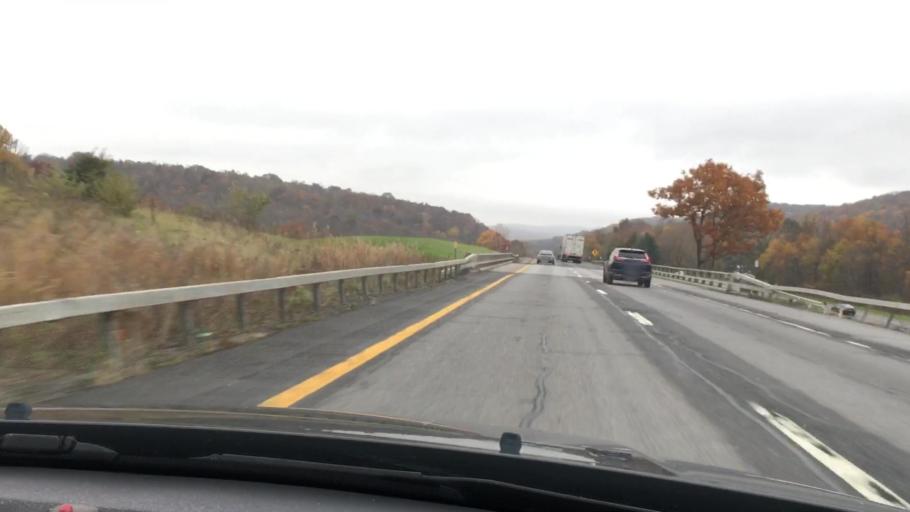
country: US
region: New York
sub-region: Putnam County
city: Lake Carmel
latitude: 41.4737
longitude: -73.6484
